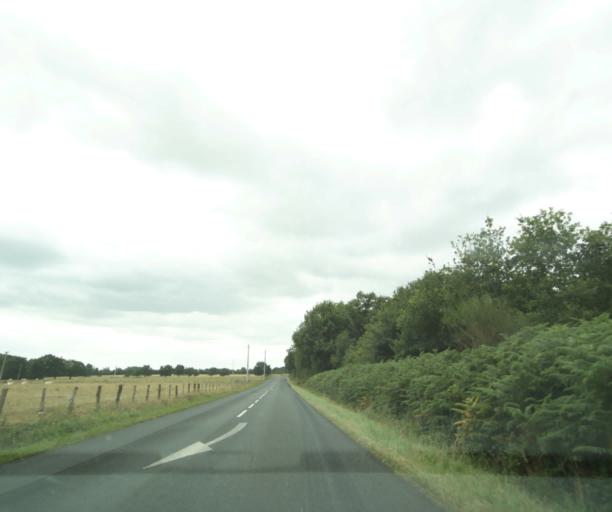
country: FR
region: Pays de la Loire
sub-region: Departement de la Sarthe
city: Precigne
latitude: 47.7998
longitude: -0.3211
